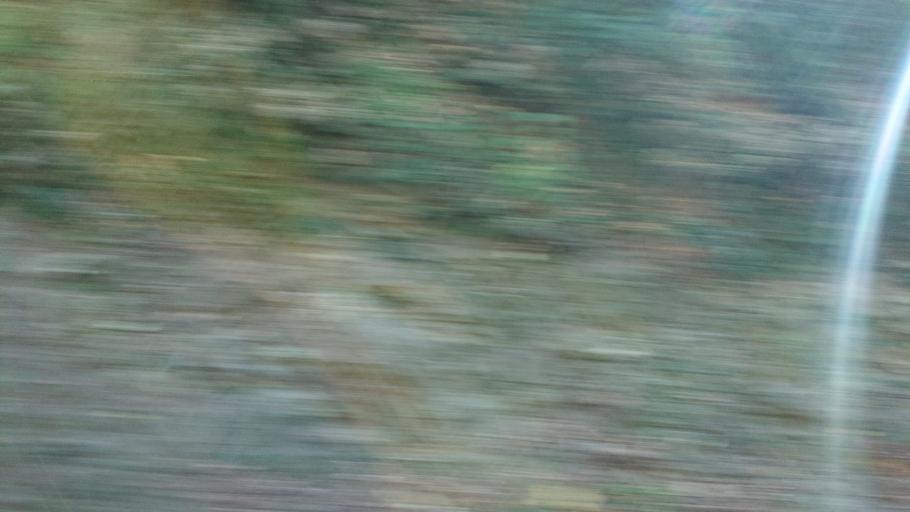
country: TW
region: Taiwan
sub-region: Hualien
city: Hualian
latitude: 24.3533
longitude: 121.3246
